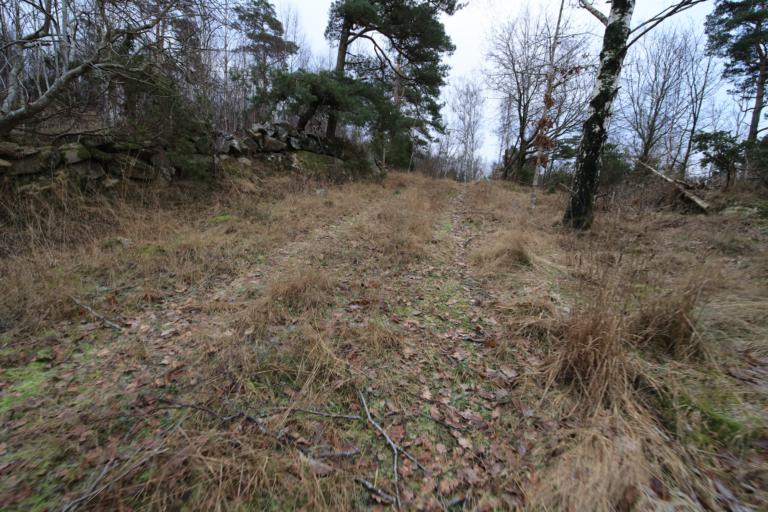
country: SE
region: Halland
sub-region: Varbergs Kommun
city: Varberg
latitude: 57.1534
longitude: 12.2873
